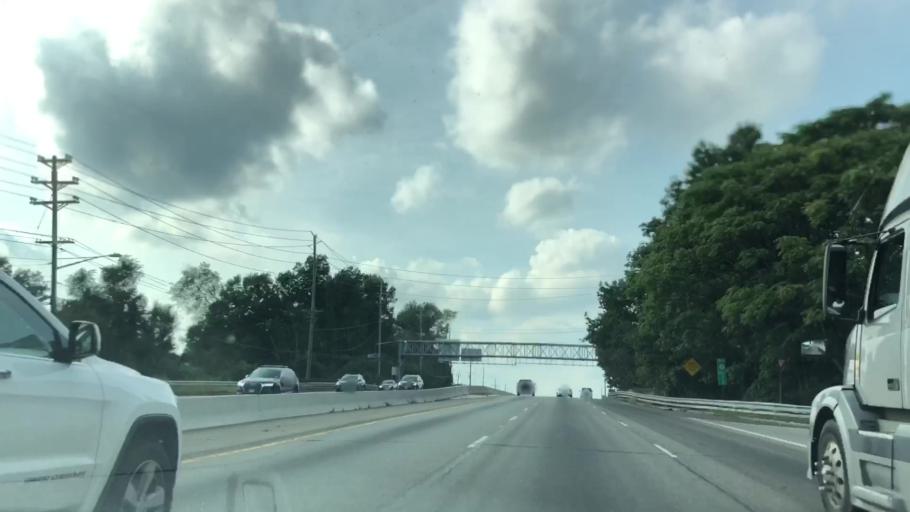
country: US
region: New Jersey
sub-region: Essex County
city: Nutley
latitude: 40.8341
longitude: -74.1476
